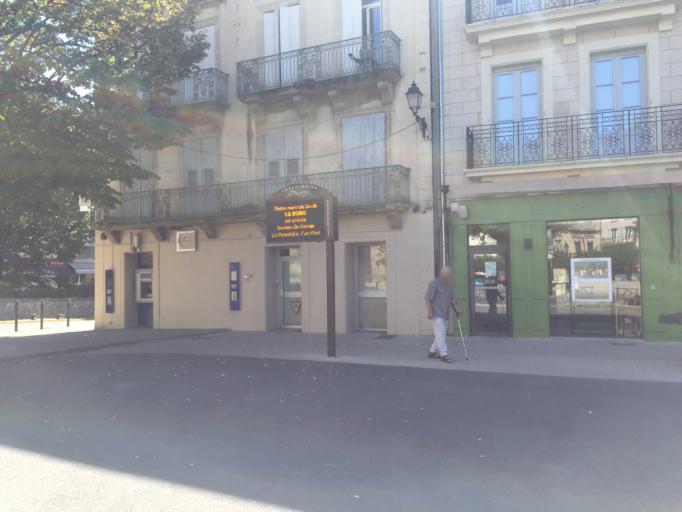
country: FR
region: Provence-Alpes-Cote d'Azur
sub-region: Departement des Alpes-de-Haute-Provence
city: Forcalquier
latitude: 43.9595
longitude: 5.7806
